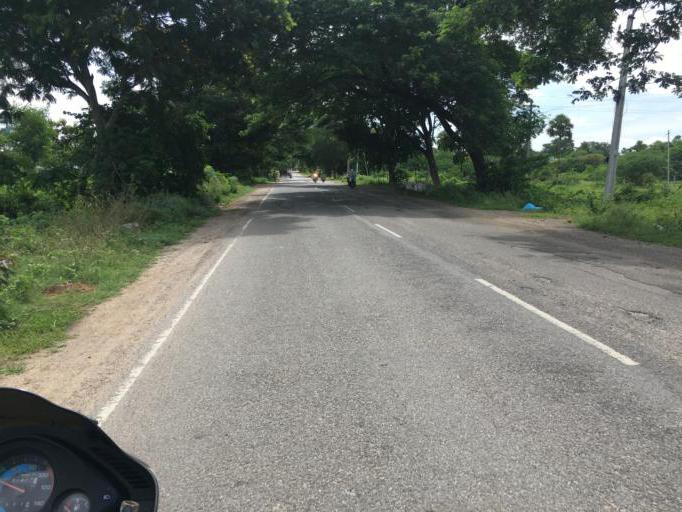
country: IN
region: Telangana
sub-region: Nalgonda
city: Nalgonda
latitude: 17.1674
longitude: 79.4101
